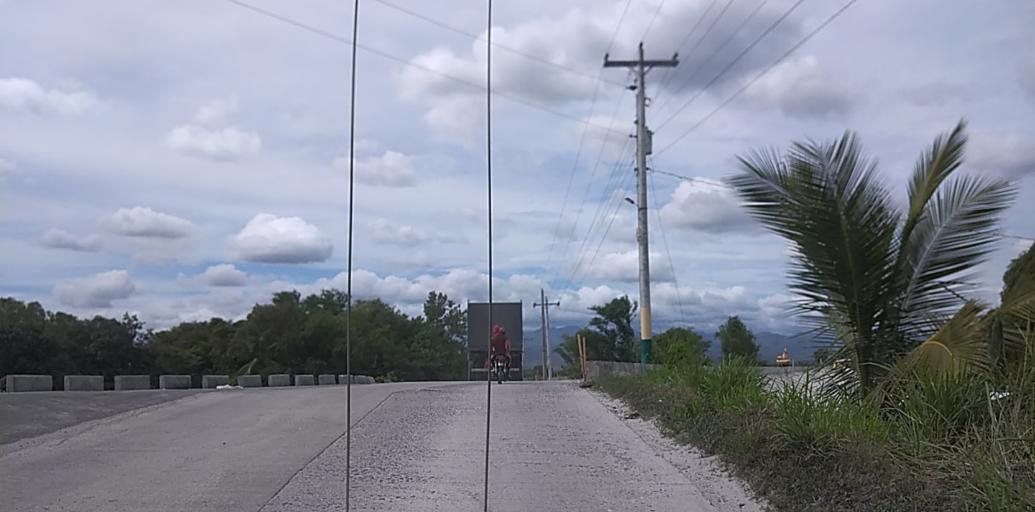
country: PH
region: Central Luzon
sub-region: Province of Pampanga
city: Porac
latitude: 15.0681
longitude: 120.5592
